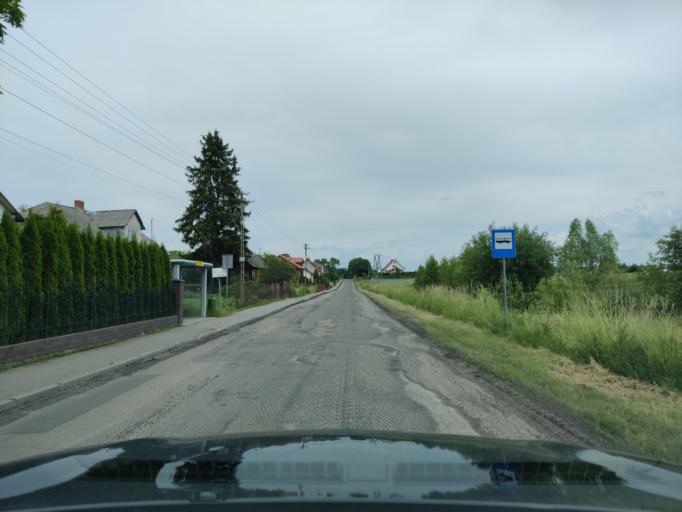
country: PL
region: Masovian Voivodeship
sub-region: Powiat wyszkowski
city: Rzasnik
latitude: 52.6850
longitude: 21.4185
